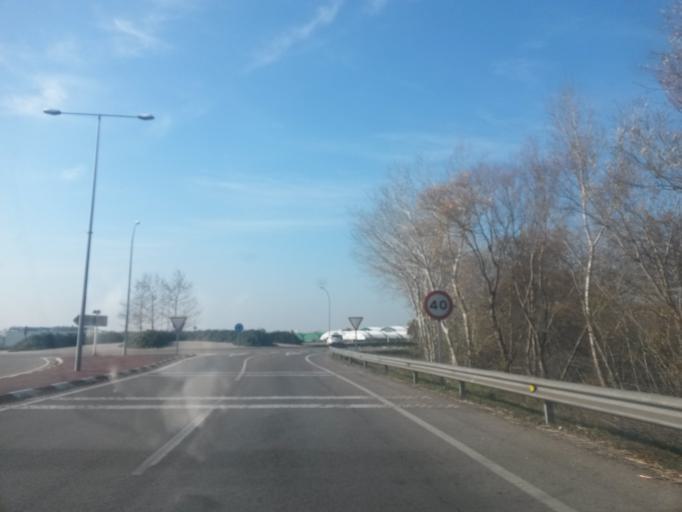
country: ES
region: Catalonia
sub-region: Provincia de Girona
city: Empuriabrava
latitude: 42.2651
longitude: 3.1119
